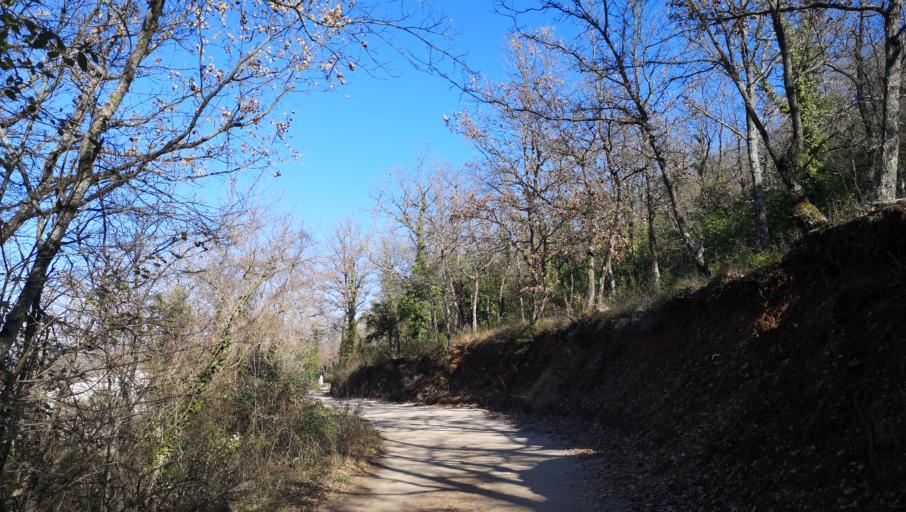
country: FR
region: Provence-Alpes-Cote d'Azur
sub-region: Departement du Var
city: Ginasservis
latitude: 43.5916
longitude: 5.8568
